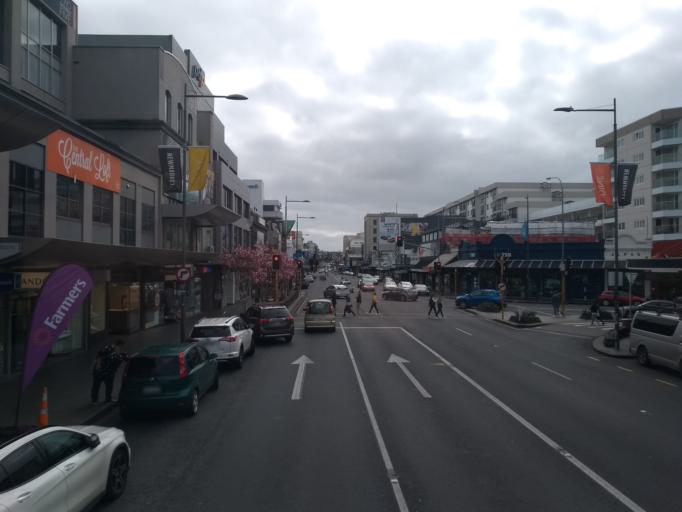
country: NZ
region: Auckland
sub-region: Auckland
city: Auckland
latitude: -36.8703
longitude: 174.7773
